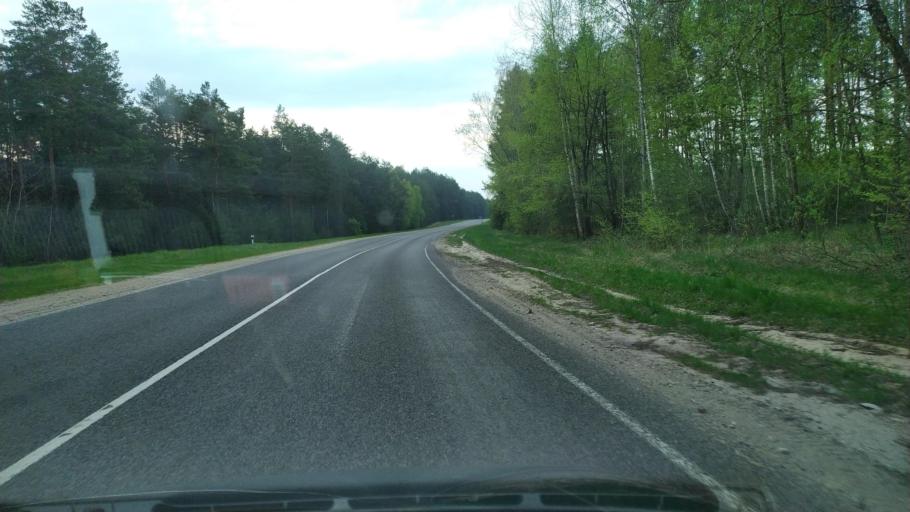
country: BY
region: Brest
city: Kamyanyets
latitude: 52.3847
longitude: 23.8571
